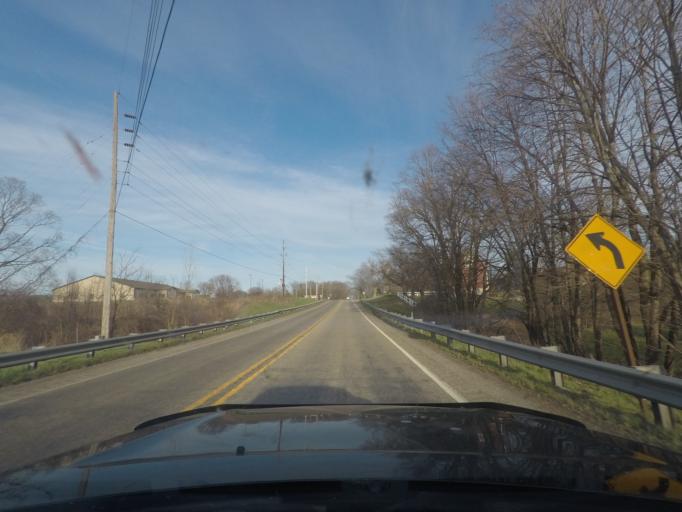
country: US
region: Indiana
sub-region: LaPorte County
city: LaPorte
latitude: 41.5912
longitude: -86.7547
